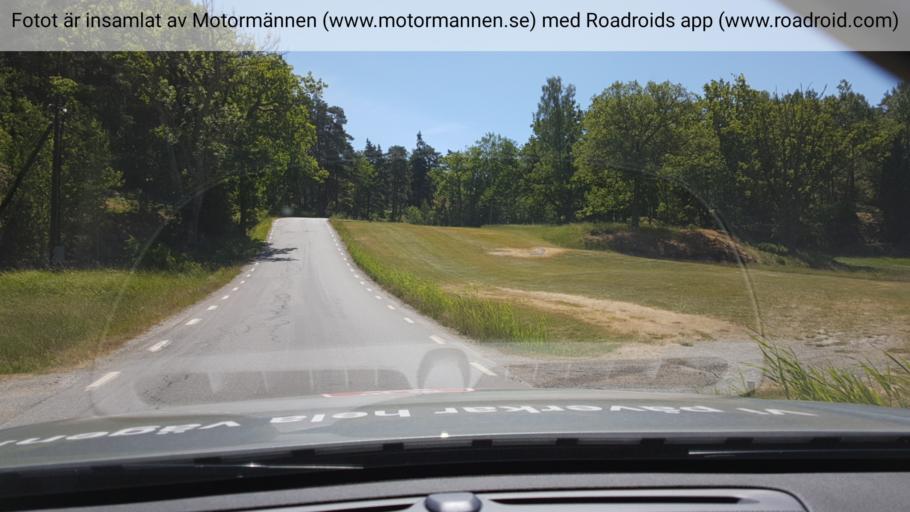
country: SE
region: Stockholm
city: Dalaro
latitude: 59.1640
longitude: 18.4481
